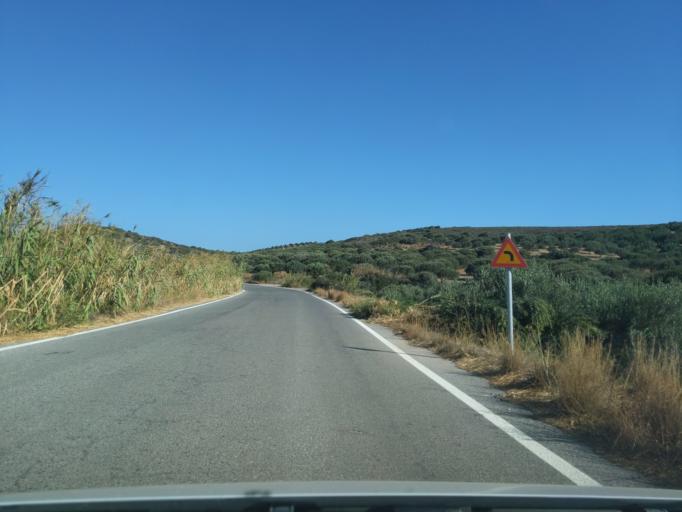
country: GR
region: Crete
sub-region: Nomos Lasithiou
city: Palekastro
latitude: 35.2224
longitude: 26.2590
